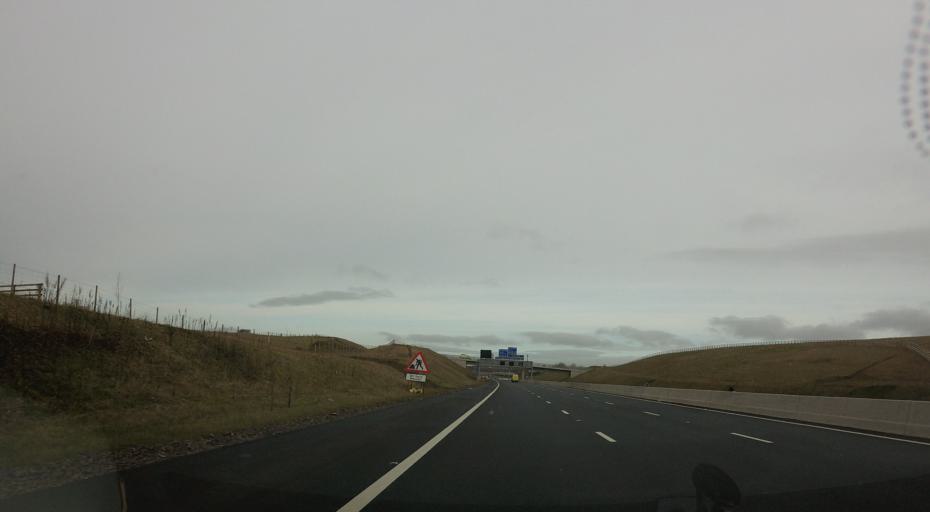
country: GB
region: Scotland
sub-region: North Lanarkshire
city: Coatbridge
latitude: 55.8418
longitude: -4.0462
